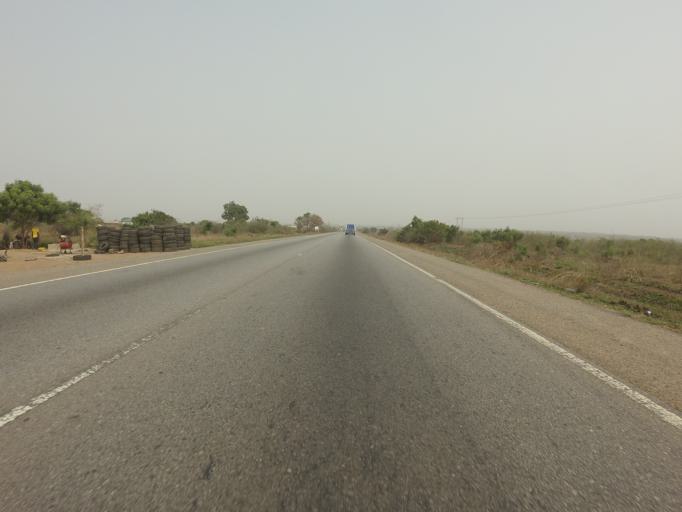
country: GH
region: Greater Accra
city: Tema
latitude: 5.8671
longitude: 0.2990
